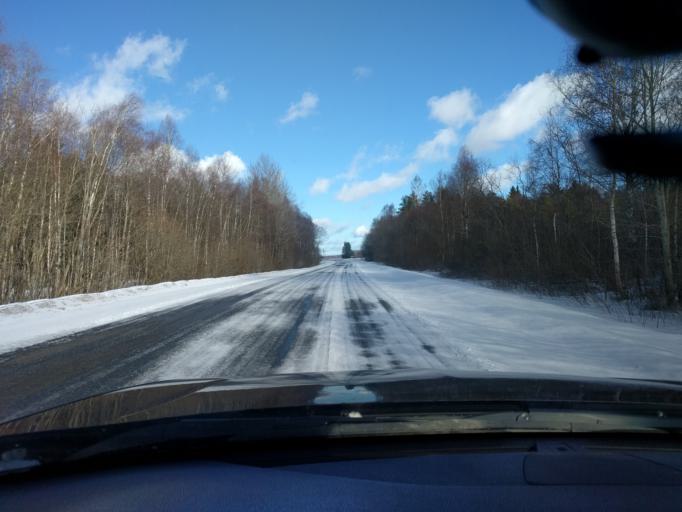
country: EE
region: Harju
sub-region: Raasiku vald
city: Raasiku
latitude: 59.3216
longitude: 25.1585
